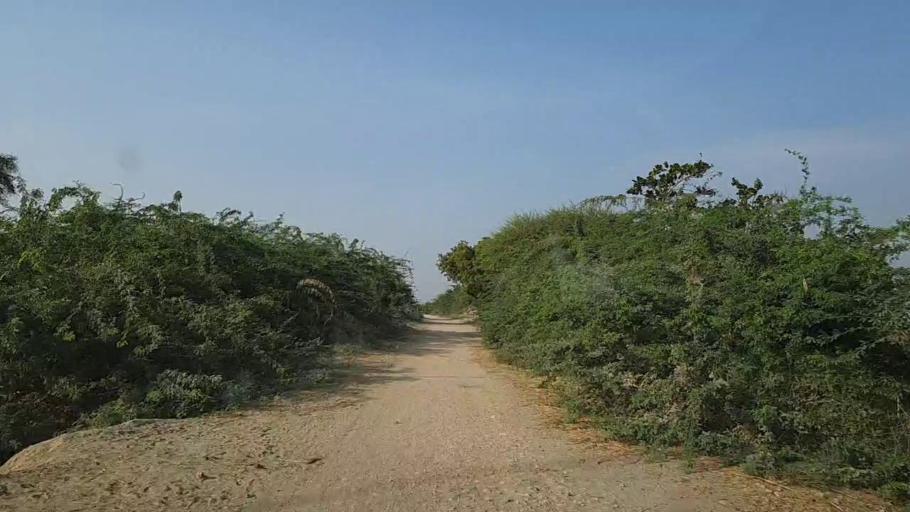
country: PK
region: Sindh
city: Mirpur Sakro
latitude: 24.5918
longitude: 67.6491
